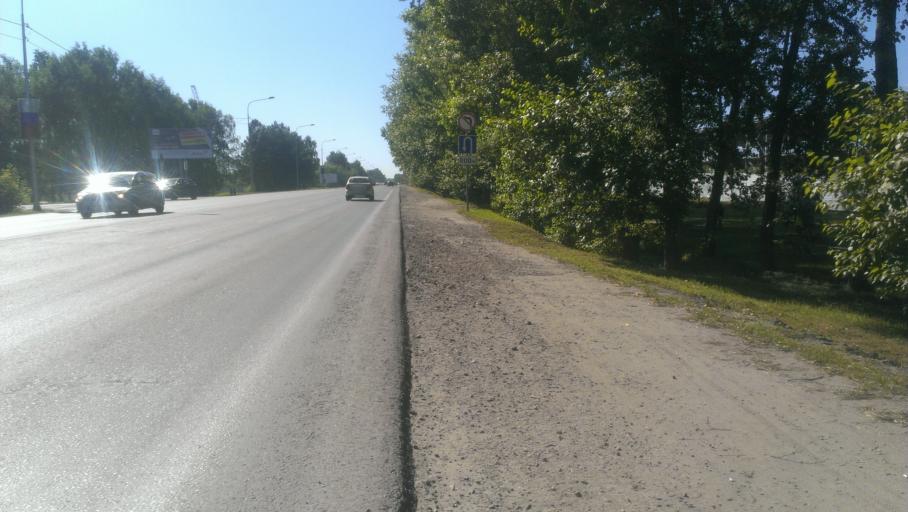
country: RU
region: Altai Krai
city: Novosilikatnyy
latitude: 53.3470
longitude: 83.6454
